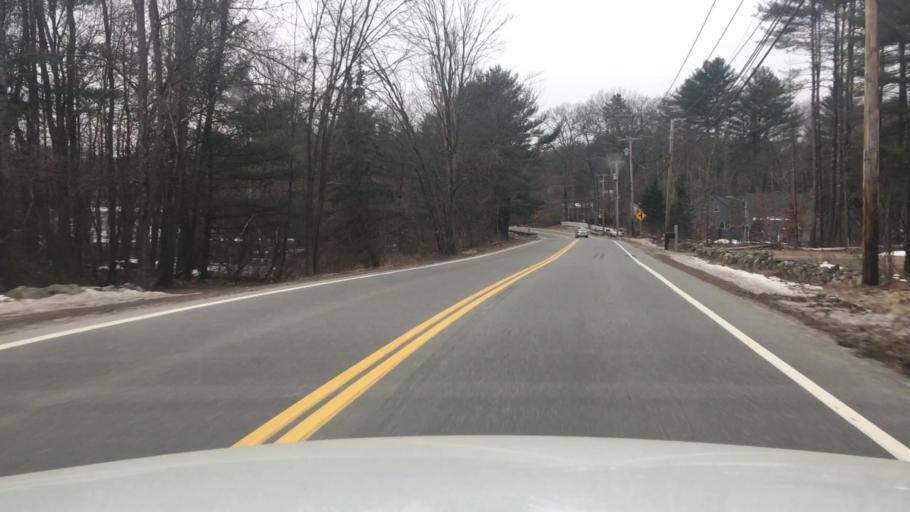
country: US
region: New Hampshire
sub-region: Merrimack County
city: Concord
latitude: 43.1559
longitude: -71.5999
